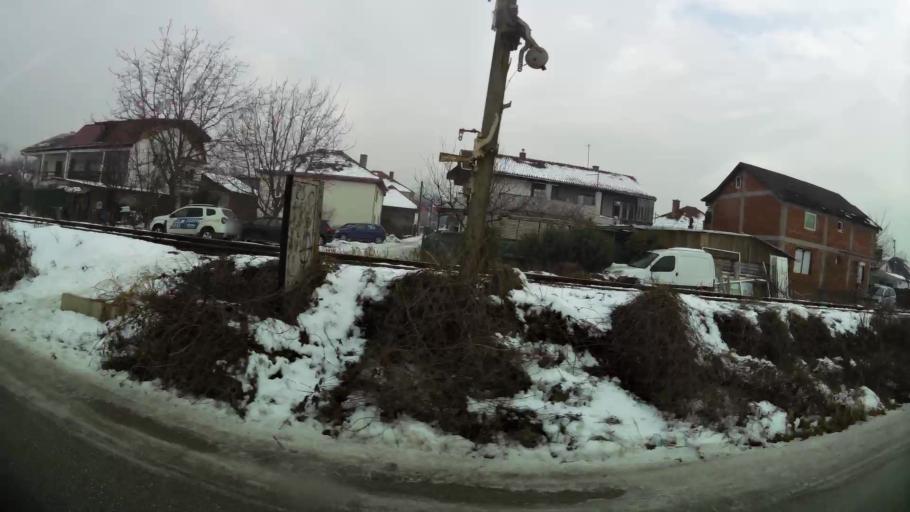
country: MK
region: Saraj
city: Saraj
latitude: 42.0358
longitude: 21.3509
